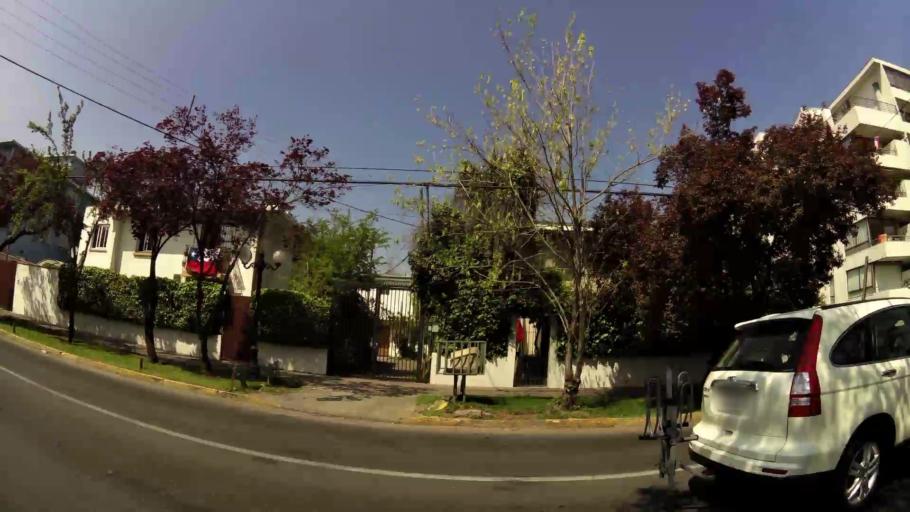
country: CL
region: Santiago Metropolitan
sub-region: Provincia de Santiago
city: Villa Presidente Frei, Nunoa, Santiago, Chile
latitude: -33.4427
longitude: -70.6010
